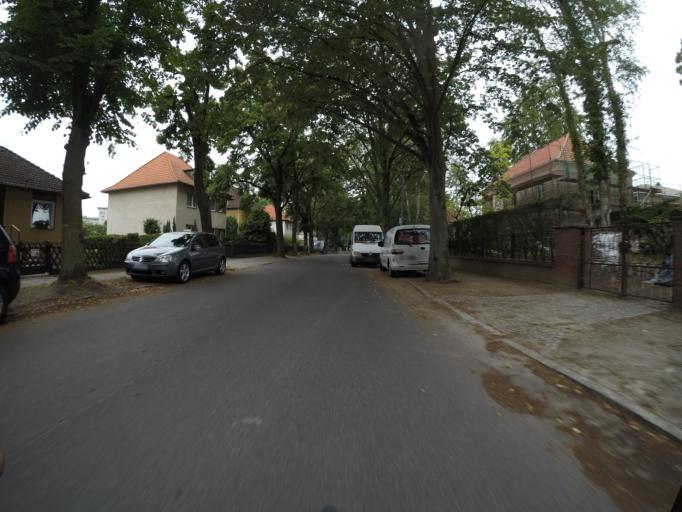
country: DE
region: Berlin
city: Tegel
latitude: 52.5924
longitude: 13.2753
